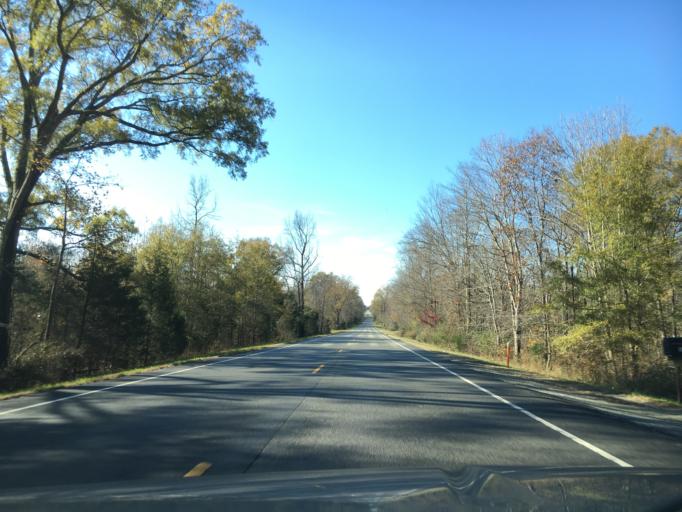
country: US
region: Virginia
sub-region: Cumberland County
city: Cumberland
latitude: 37.5146
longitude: -78.2154
